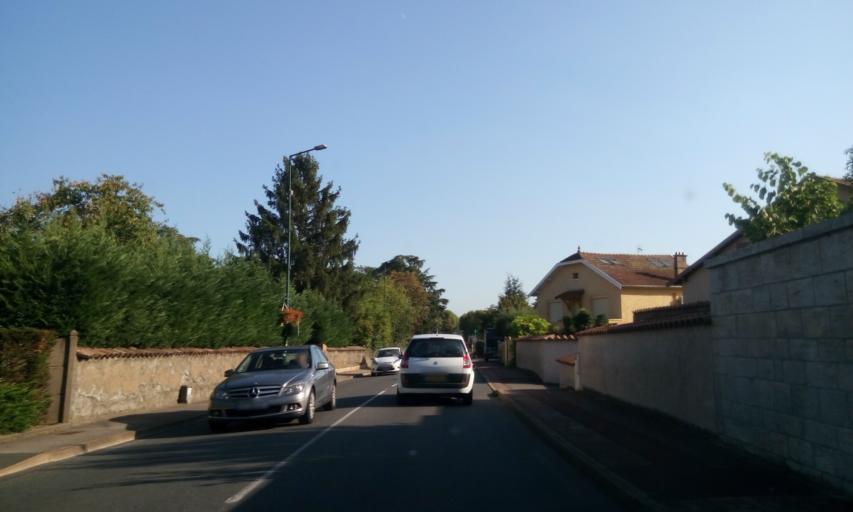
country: FR
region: Rhone-Alpes
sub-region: Departement du Rhone
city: Morance
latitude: 45.8787
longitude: 4.7097
